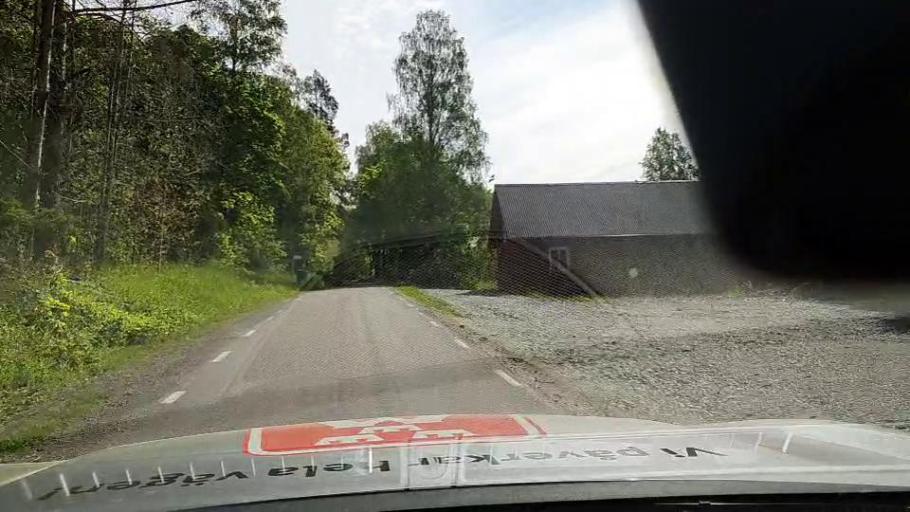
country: SE
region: Soedermanland
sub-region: Eskilstuna Kommun
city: Arla
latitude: 59.2570
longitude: 16.6975
